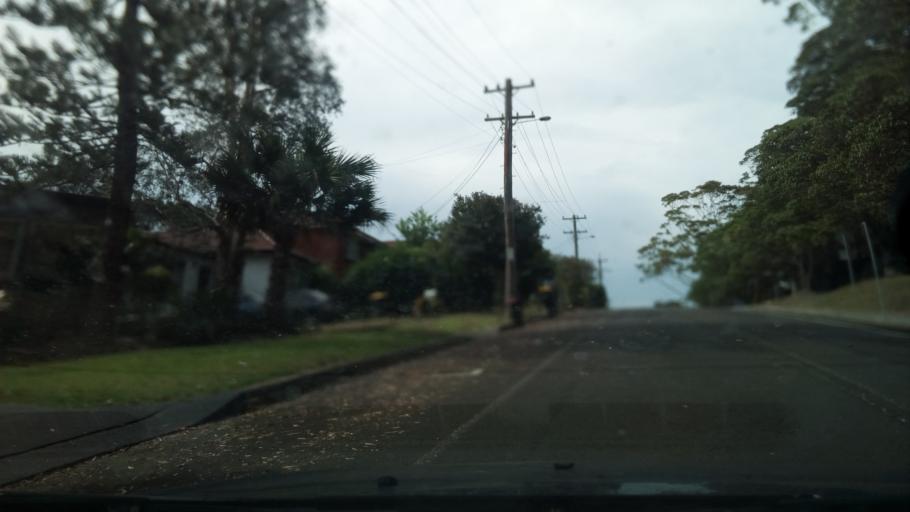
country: AU
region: New South Wales
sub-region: Wollongong
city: Keiraville
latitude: -34.4105
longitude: 150.8712
